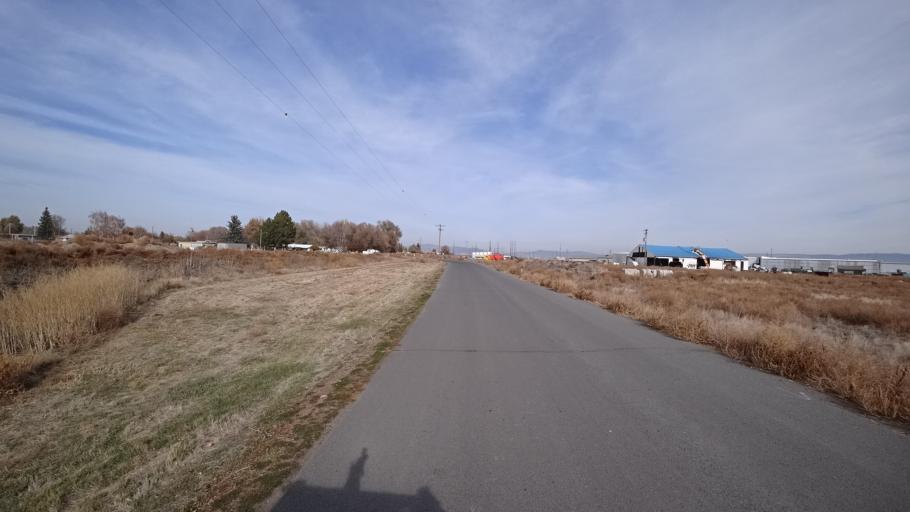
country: US
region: California
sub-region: Siskiyou County
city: Tulelake
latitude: 41.9499
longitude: -121.4714
